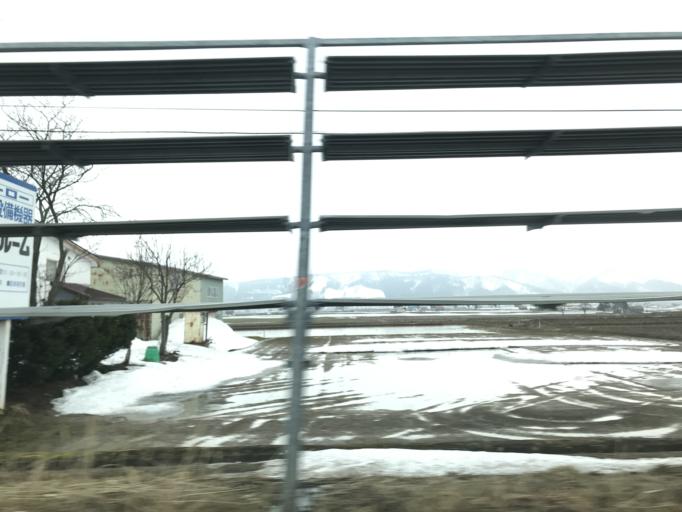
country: JP
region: Hokkaido
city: Nayoro
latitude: 44.2281
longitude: 142.3948
